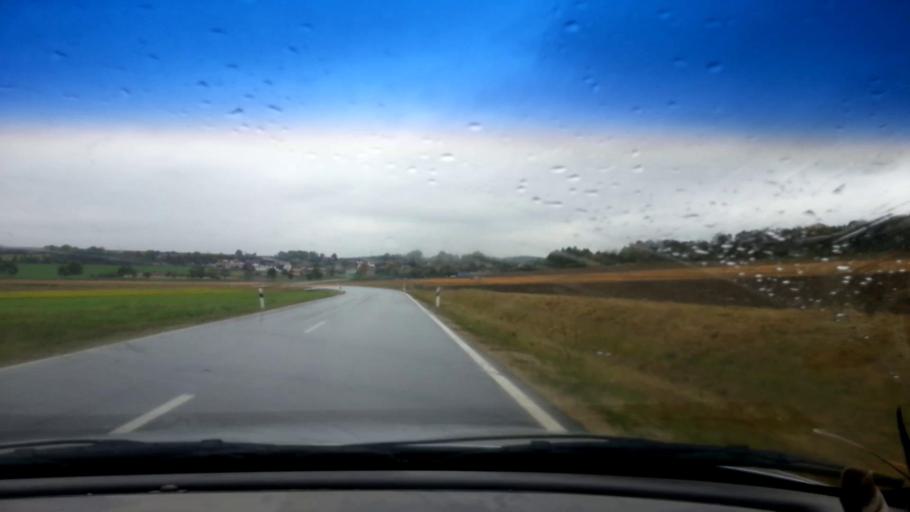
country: DE
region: Bavaria
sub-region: Upper Franconia
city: Konigsfeld
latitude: 49.9383
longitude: 11.1559
